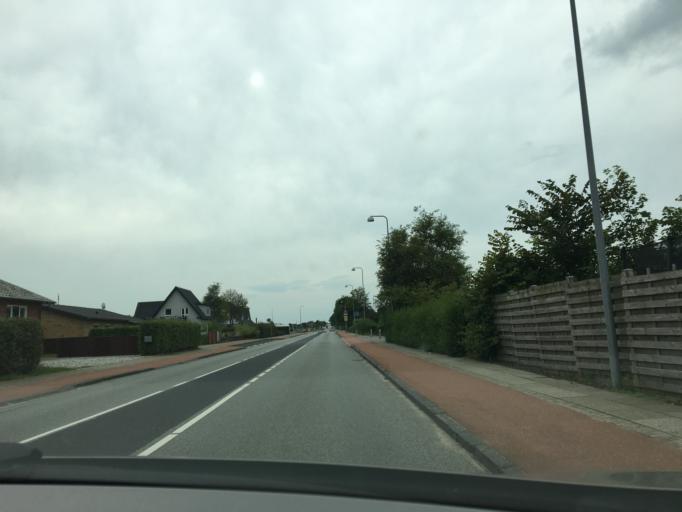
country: DK
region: Central Jutland
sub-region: Ringkobing-Skjern Kommune
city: Videbaek
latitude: 56.0911
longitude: 8.6205
